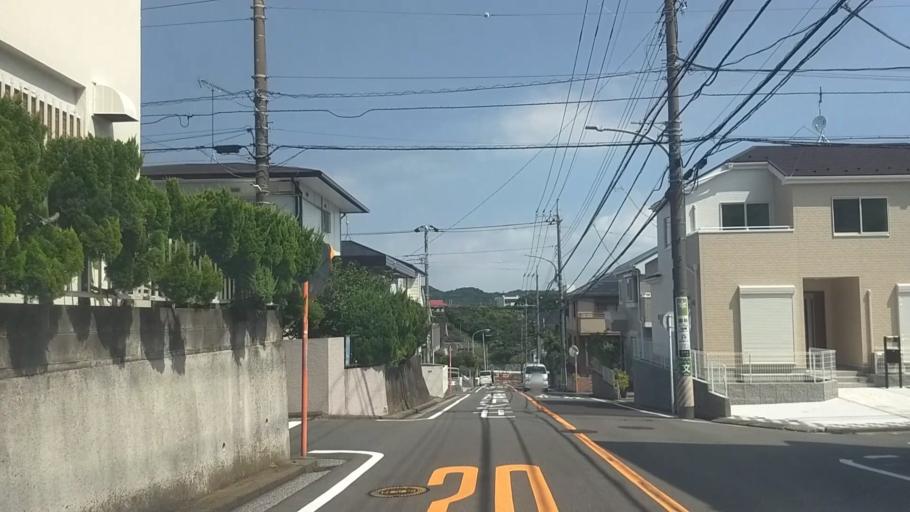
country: JP
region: Kanagawa
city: Zushi
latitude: 35.3334
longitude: 139.6038
